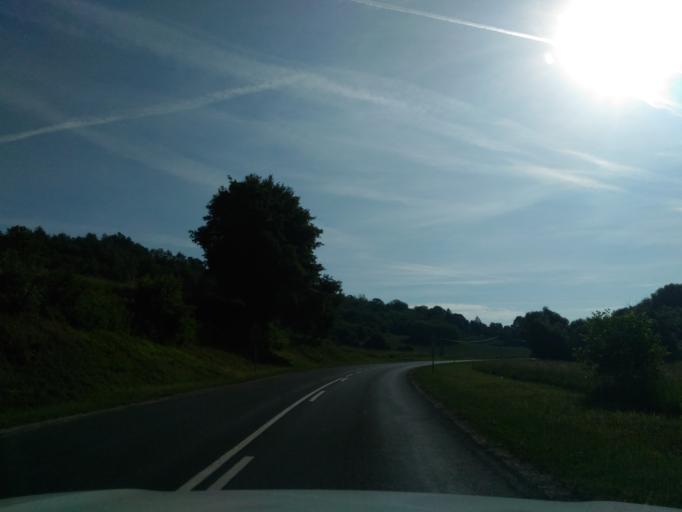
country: HU
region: Baranya
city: Komlo
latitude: 46.1604
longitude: 18.2280
